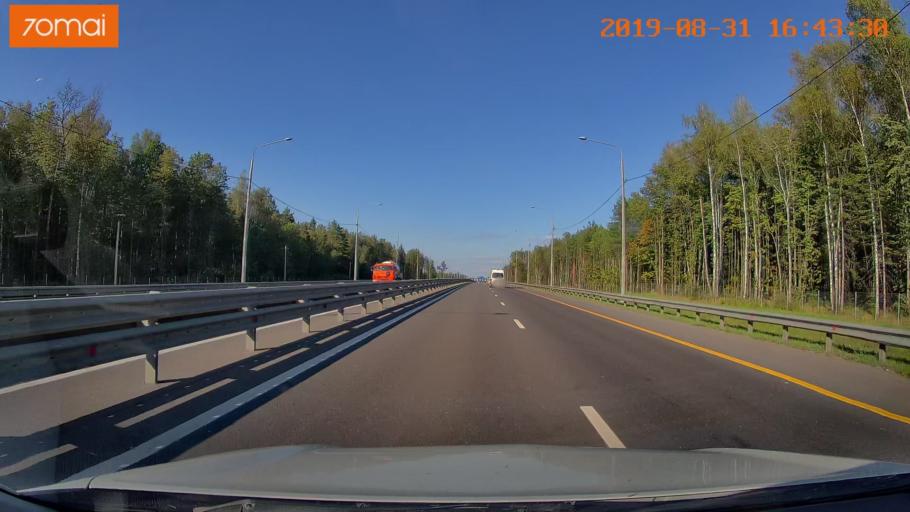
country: RU
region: Kaluga
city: Mstikhino
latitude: 54.6104
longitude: 36.1058
